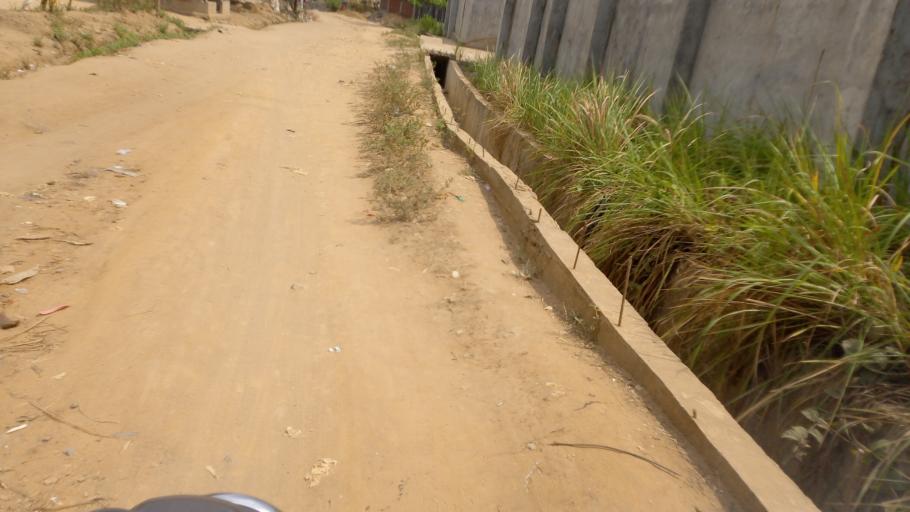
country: SL
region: Western Area
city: Waterloo
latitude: 8.3114
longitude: -13.0655
